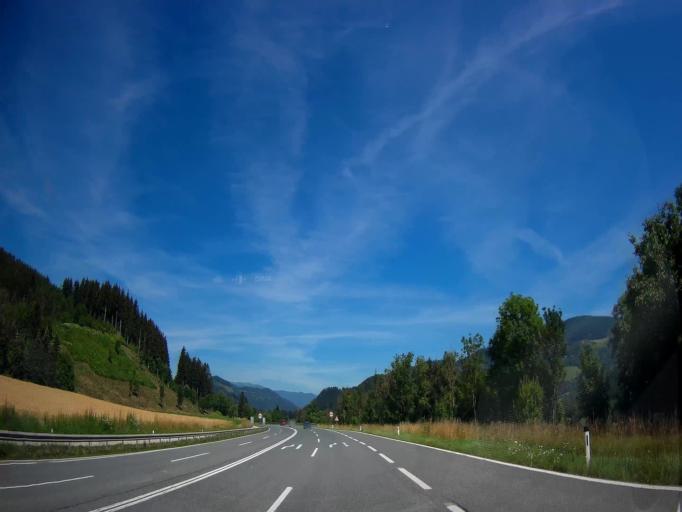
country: AT
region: Carinthia
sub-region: Politischer Bezirk Sankt Veit an der Glan
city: Althofen
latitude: 46.8778
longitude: 14.4509
